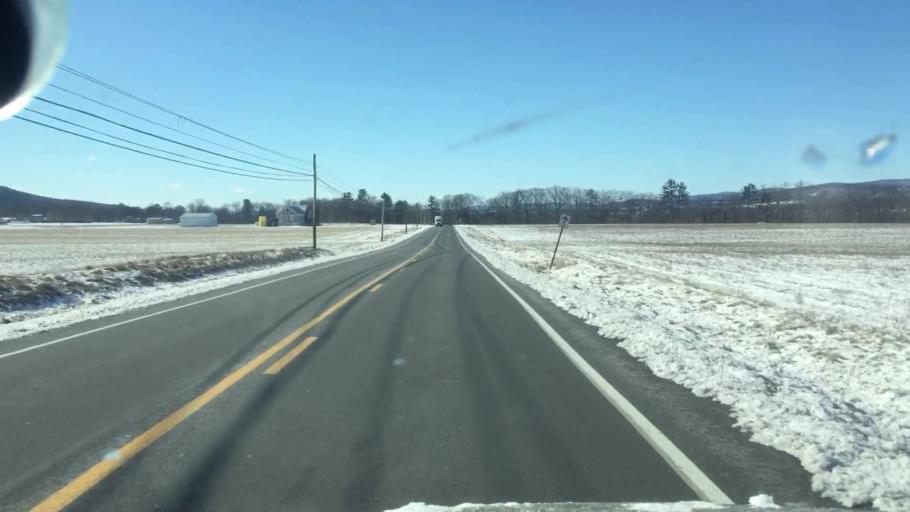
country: US
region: Pennsylvania
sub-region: Luzerne County
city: Nescopeck
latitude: 41.0552
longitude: -76.1949
